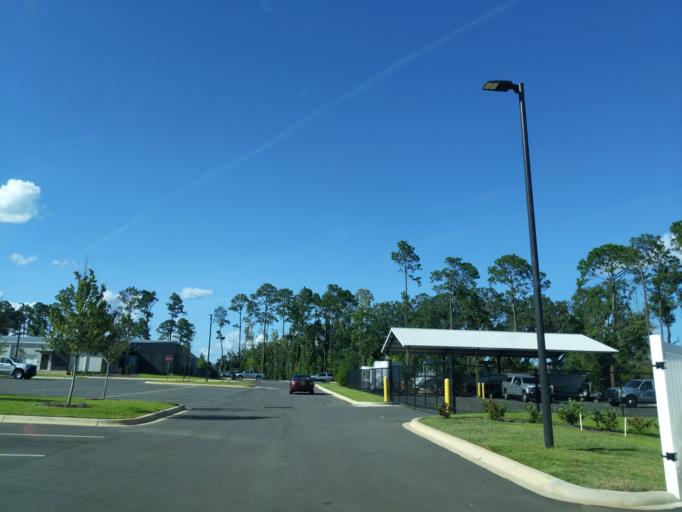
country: US
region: Florida
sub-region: Leon County
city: Tallahassee
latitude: 30.4087
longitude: -84.2447
